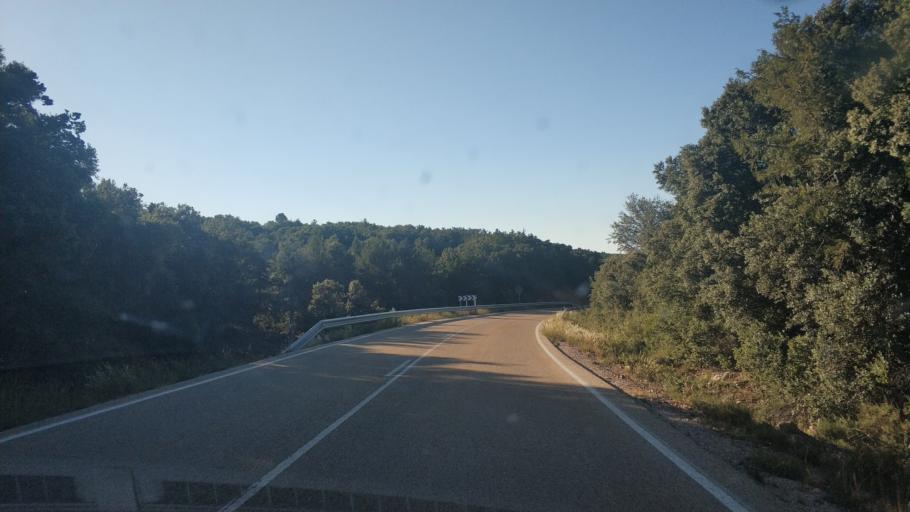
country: ES
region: Castille and Leon
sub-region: Provincia de Soria
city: Montejo de Tiermes
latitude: 41.4168
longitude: -3.2041
